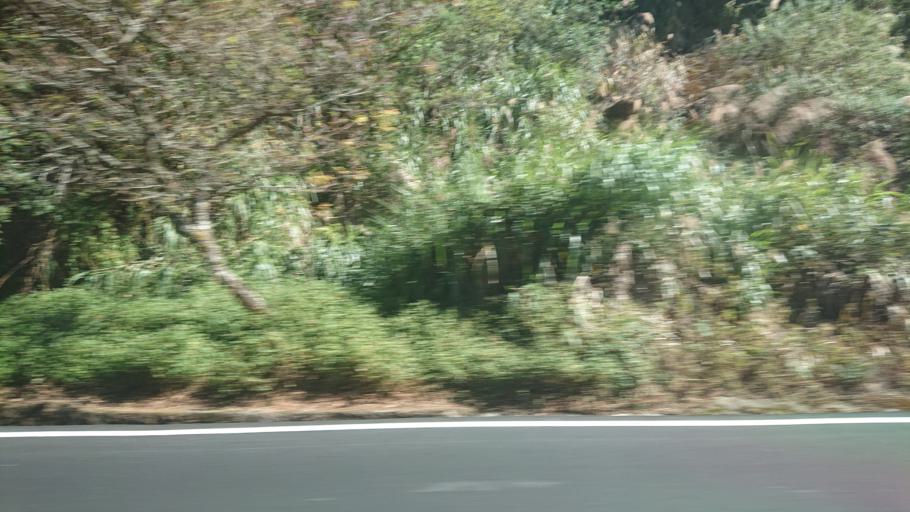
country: TW
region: Taiwan
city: Lugu
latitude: 23.4965
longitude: 120.8198
